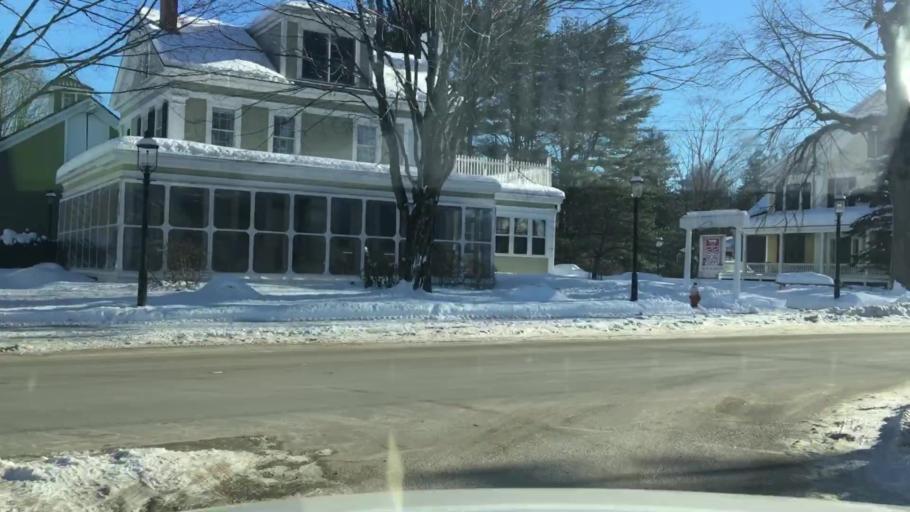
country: US
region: Maine
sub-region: Oxford County
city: Bethel
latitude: 44.4031
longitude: -70.7899
